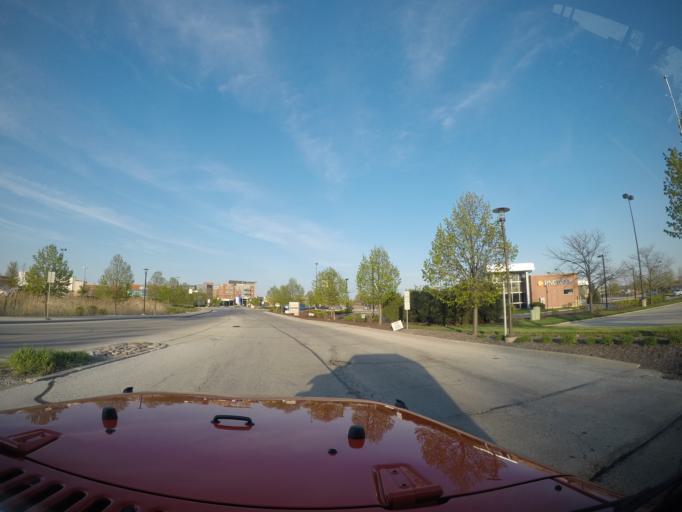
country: US
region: Illinois
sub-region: Cook County
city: Prospect Heights
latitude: 42.0832
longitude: -87.9364
